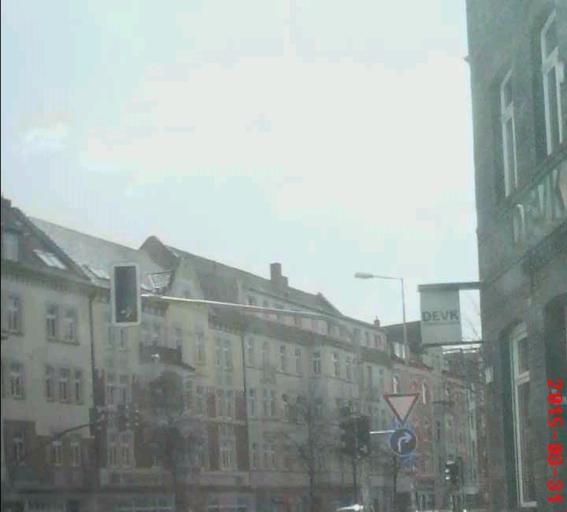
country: DE
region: Thuringia
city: Erfurt
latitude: 50.9993
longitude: 11.0259
